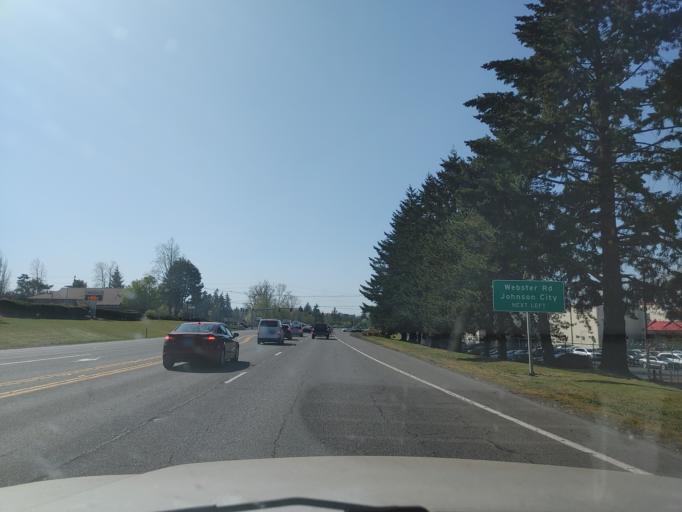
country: US
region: Oregon
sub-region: Clackamas County
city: Oatfield
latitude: 45.4243
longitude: -122.5904
